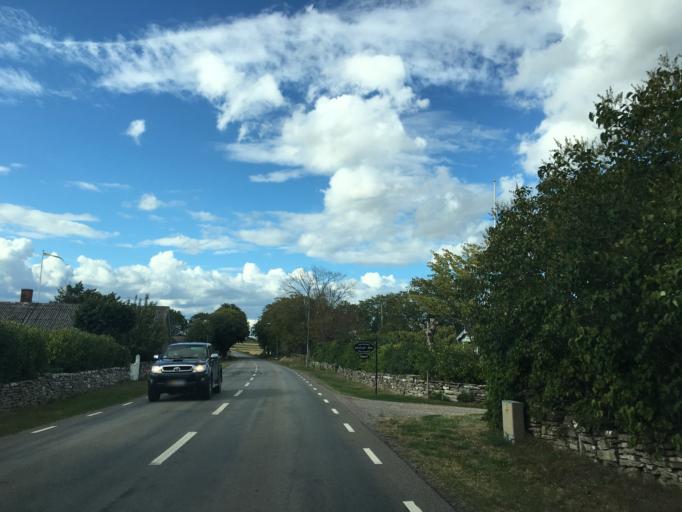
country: SE
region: Kalmar
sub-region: Morbylanga Kommun
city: Moerbylanga
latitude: 56.4611
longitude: 16.4304
